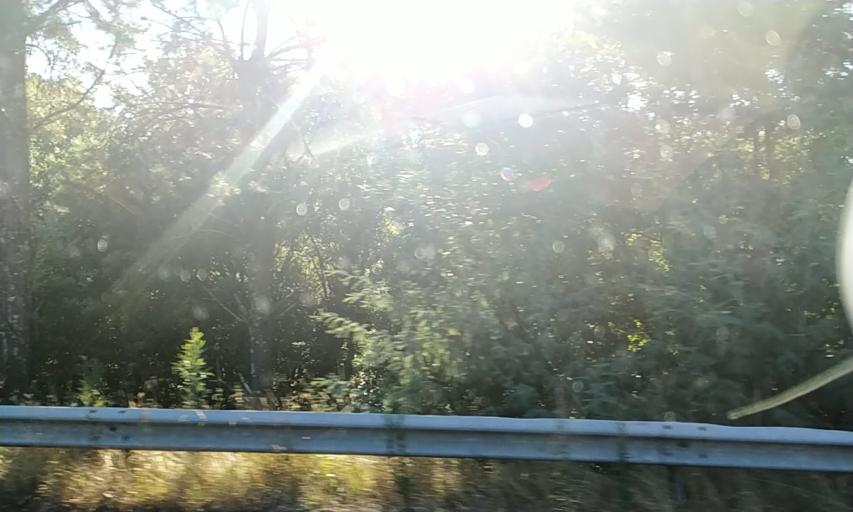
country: PT
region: Porto
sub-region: Santo Tirso
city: Sao Miguel do Couto
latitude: 41.3137
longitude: -8.4704
